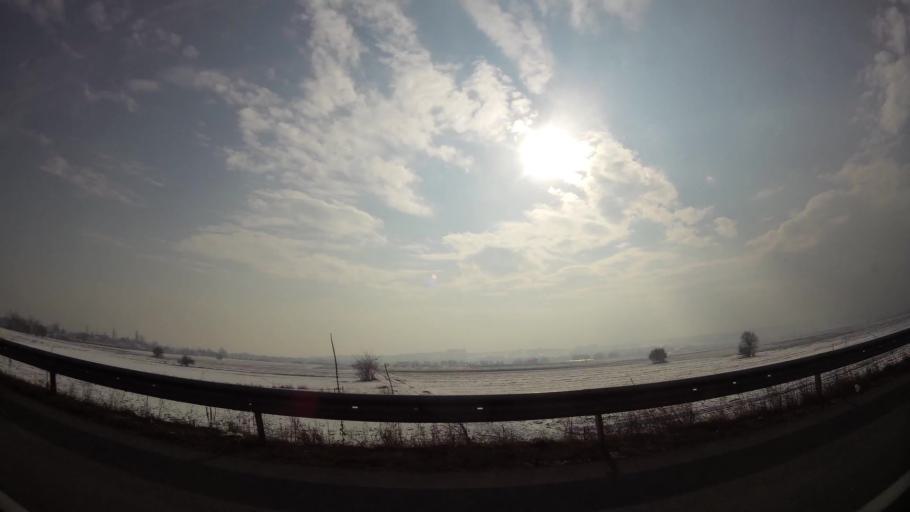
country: MK
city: Creshevo
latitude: 42.0308
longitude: 21.5053
